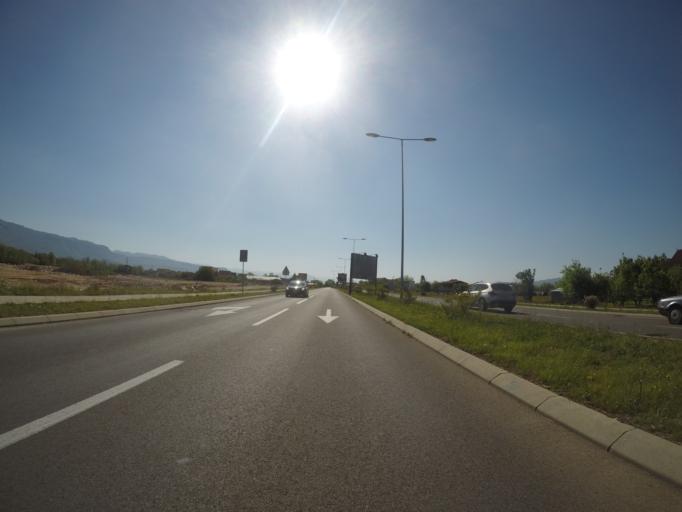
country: ME
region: Danilovgrad
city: Danilovgrad
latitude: 42.5463
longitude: 19.1010
